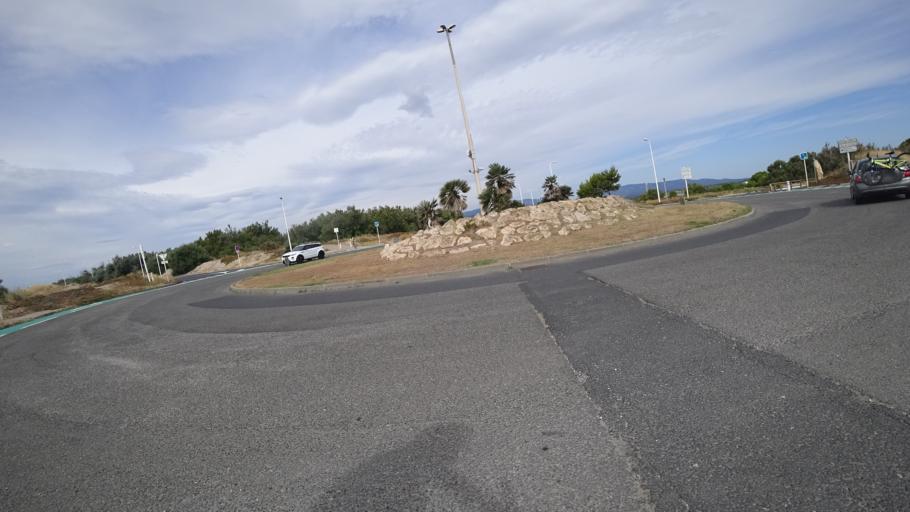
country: FR
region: Languedoc-Roussillon
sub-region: Departement de l'Aude
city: Leucate
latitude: 42.8823
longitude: 3.0469
